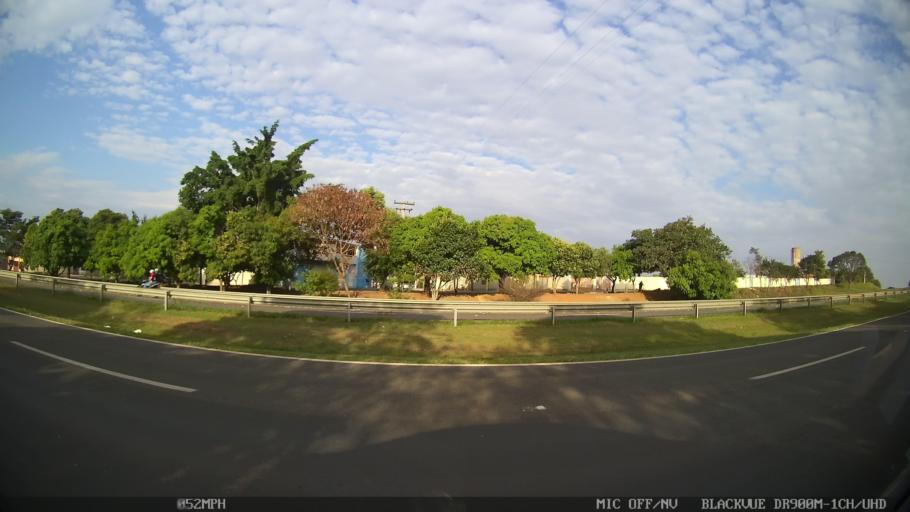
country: BR
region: Sao Paulo
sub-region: Cosmopolis
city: Cosmopolis
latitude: -22.6303
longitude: -47.2048
